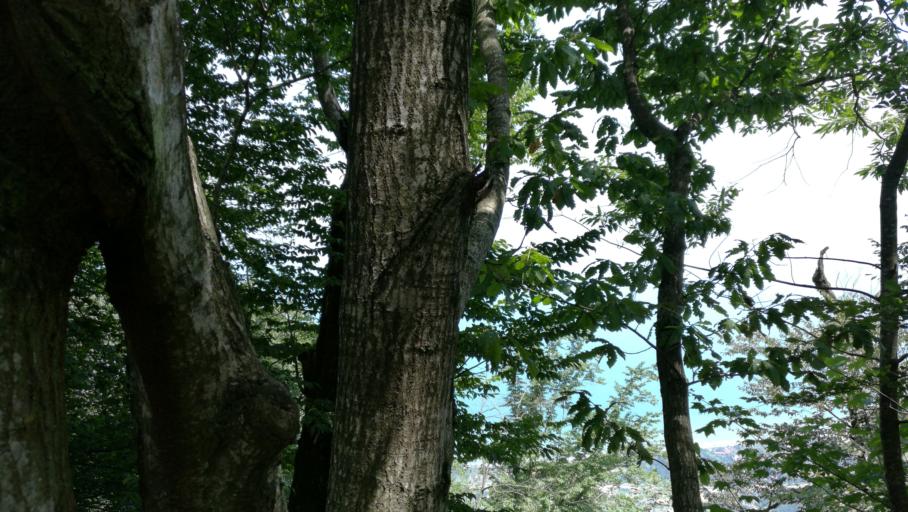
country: IR
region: Mazandaran
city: Ramsar
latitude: 36.9450
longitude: 50.6003
